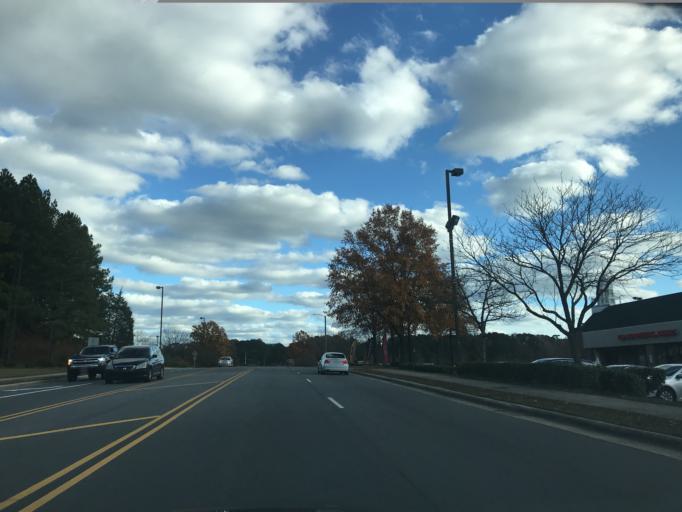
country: US
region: North Carolina
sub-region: Wake County
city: Raleigh
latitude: 35.8365
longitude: -78.5860
